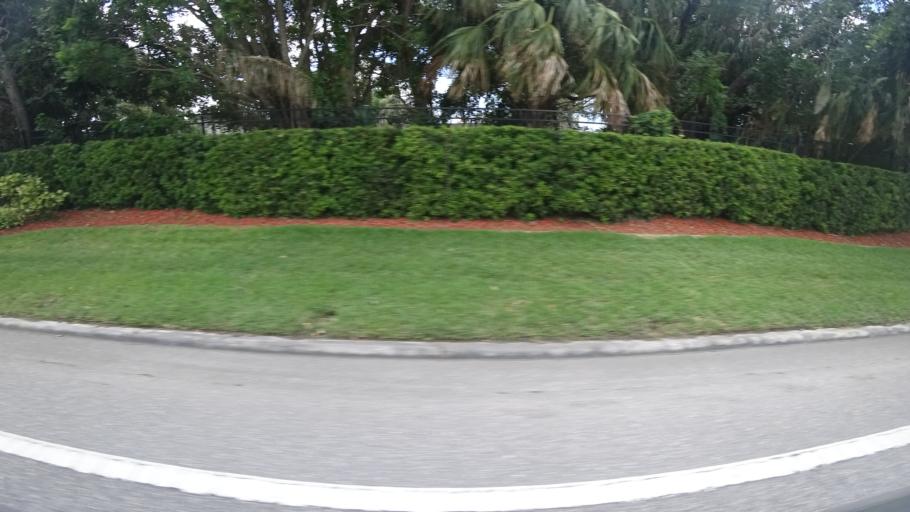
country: US
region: Florida
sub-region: Manatee County
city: Bayshore Gardens
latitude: 27.4293
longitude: -82.6005
